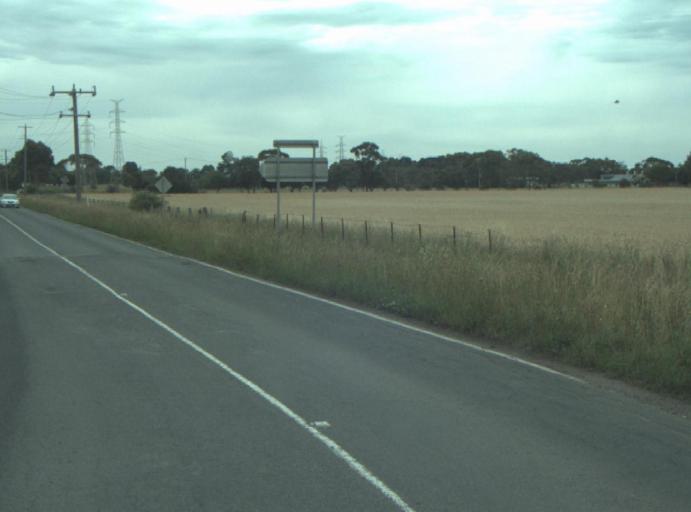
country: AU
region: Victoria
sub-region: Greater Geelong
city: Leopold
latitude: -38.1844
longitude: 144.4191
